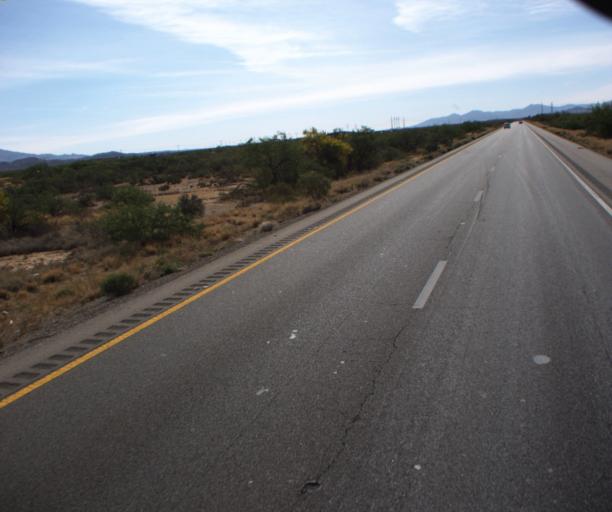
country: US
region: Arizona
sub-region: Pima County
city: Vail
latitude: 32.0422
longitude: -110.7433
